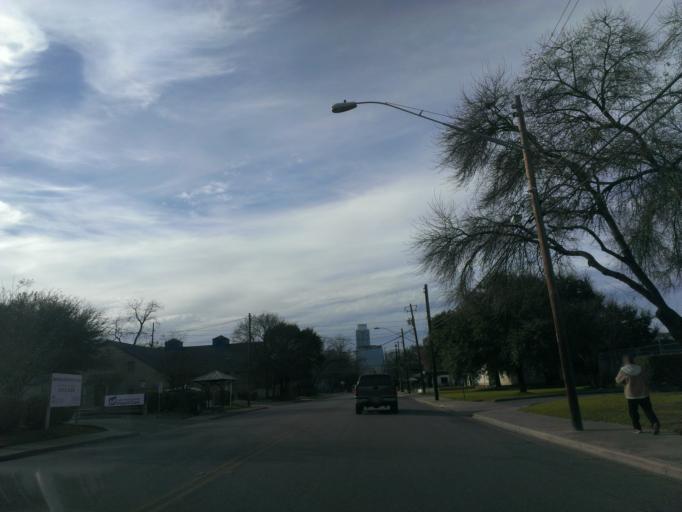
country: US
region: Texas
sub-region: Travis County
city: Austin
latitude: 30.2590
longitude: -97.7268
